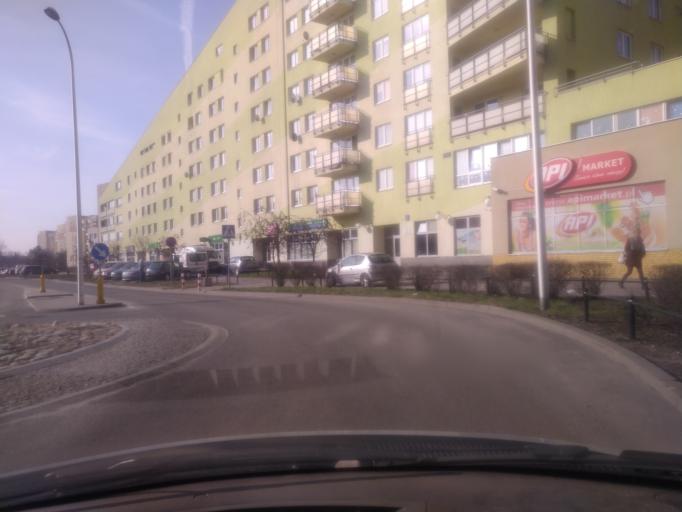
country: PL
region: Masovian Voivodeship
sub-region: Warszawa
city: Praga Poludnie
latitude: 52.2324
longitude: 21.0830
